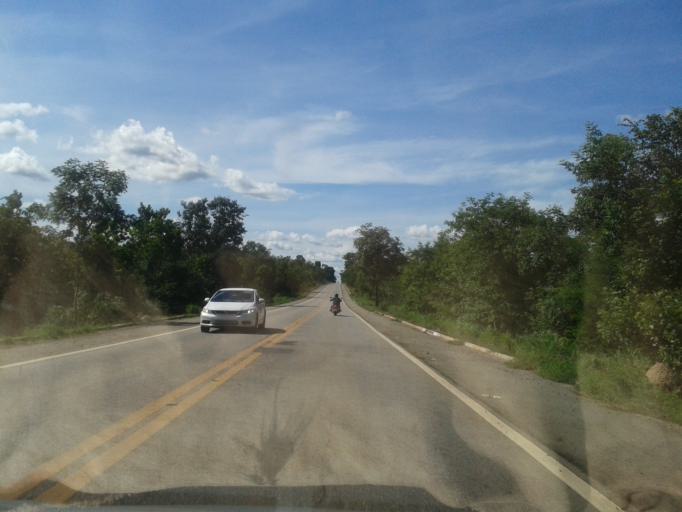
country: BR
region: Goias
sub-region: Mozarlandia
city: Mozarlandia
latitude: -15.2878
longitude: -50.4703
